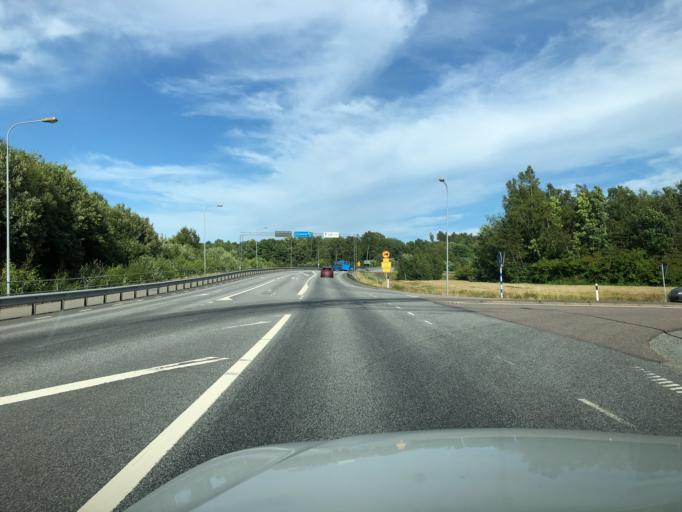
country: SE
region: Vaestra Goetaland
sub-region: Marks Kommun
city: Kinna
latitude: 57.4965
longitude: 12.6867
